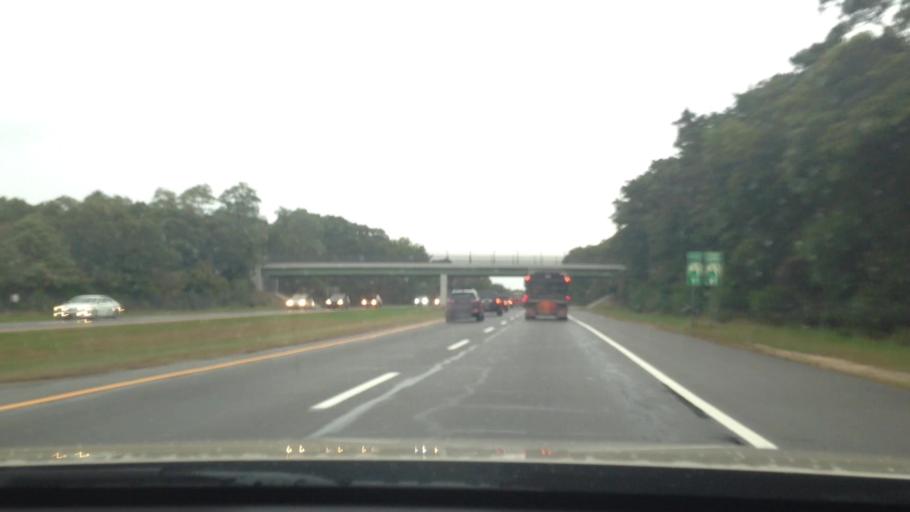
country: US
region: New York
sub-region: Suffolk County
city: Holtsville
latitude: 40.8249
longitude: -73.0546
